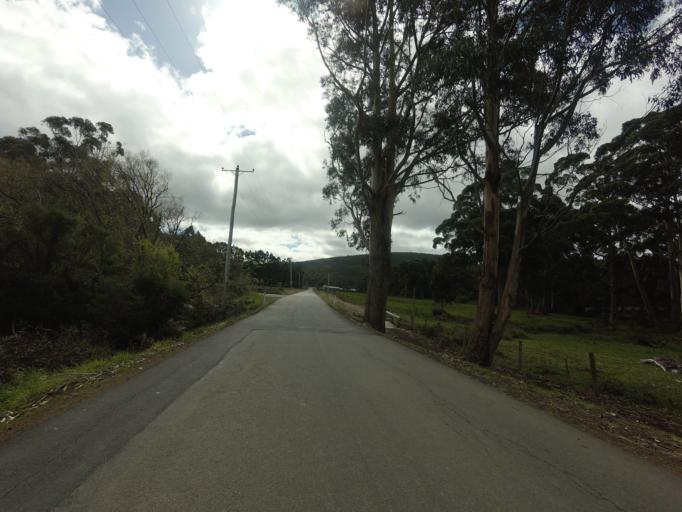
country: AU
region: Tasmania
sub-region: Huon Valley
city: Geeveston
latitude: -43.4286
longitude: 146.9733
